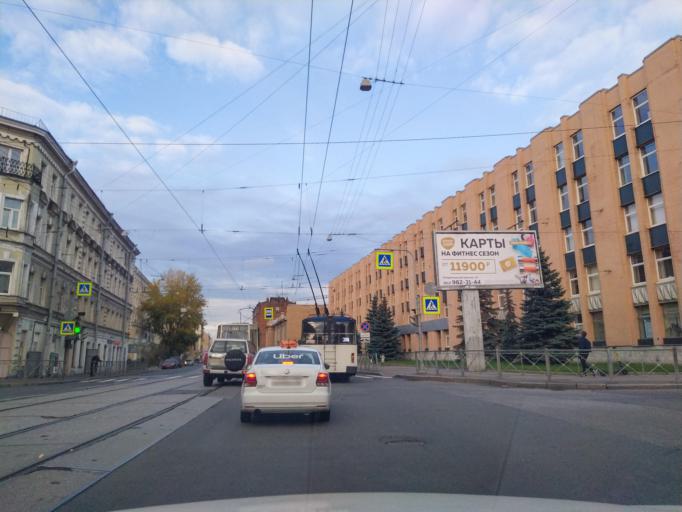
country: RU
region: Leningrad
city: Finlyandskiy
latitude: 59.9625
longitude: 30.3792
